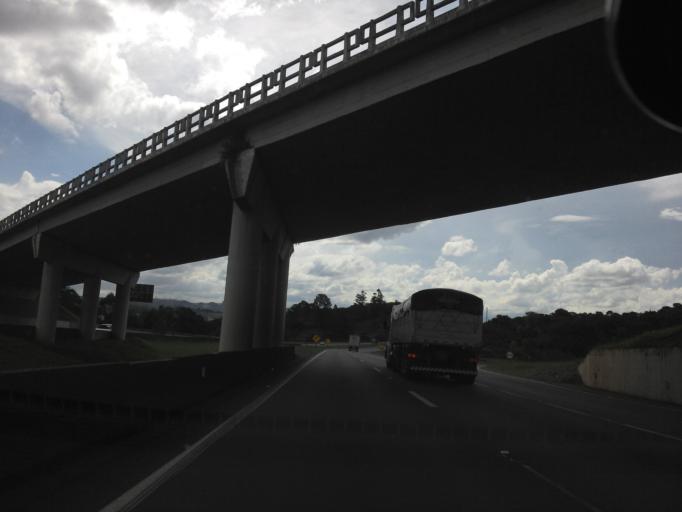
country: BR
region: Sao Paulo
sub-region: Itatiba
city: Itatiba
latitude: -22.9758
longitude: -46.8332
